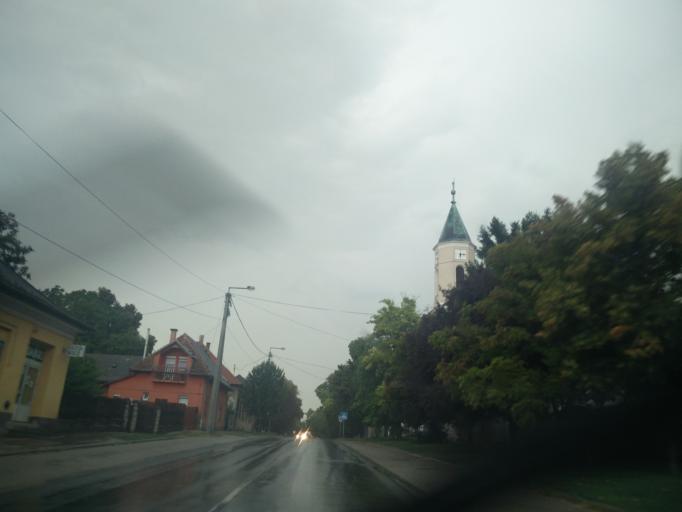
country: HU
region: Pest
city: Biatorbagy
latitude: 47.4623
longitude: 18.8113
